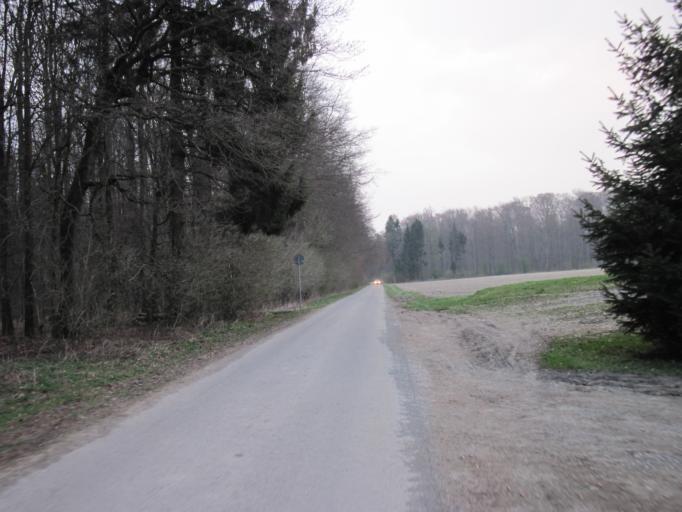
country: DE
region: North Rhine-Westphalia
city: Lichtenau
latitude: 51.6795
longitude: 8.8569
